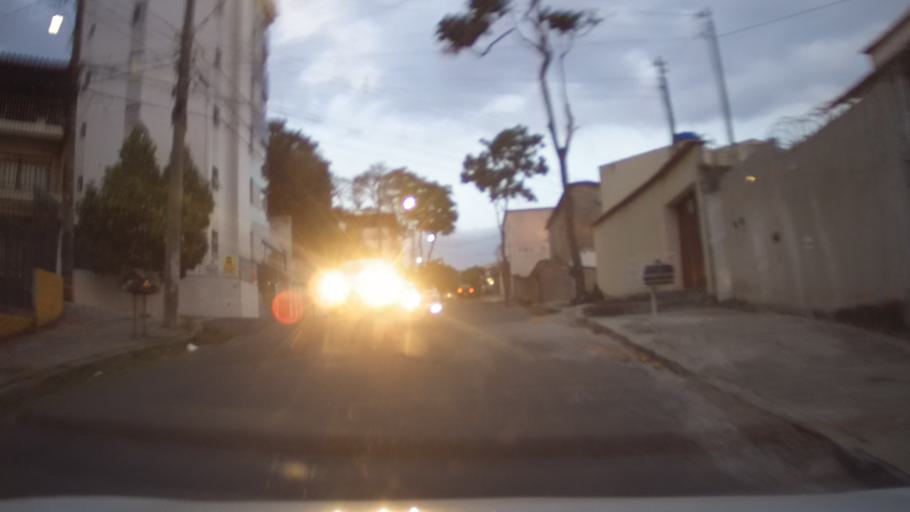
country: BR
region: Minas Gerais
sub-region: Belo Horizonte
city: Belo Horizonte
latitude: -19.8896
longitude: -43.9338
